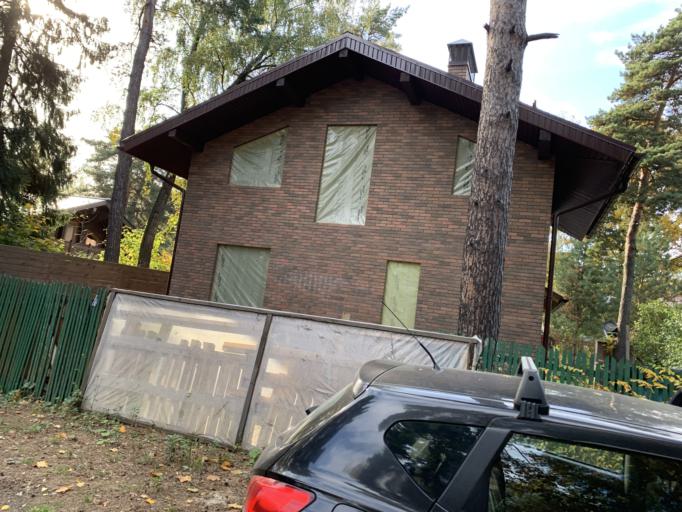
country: RU
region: Moskovskaya
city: Mamontovka
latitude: 55.9866
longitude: 37.8314
